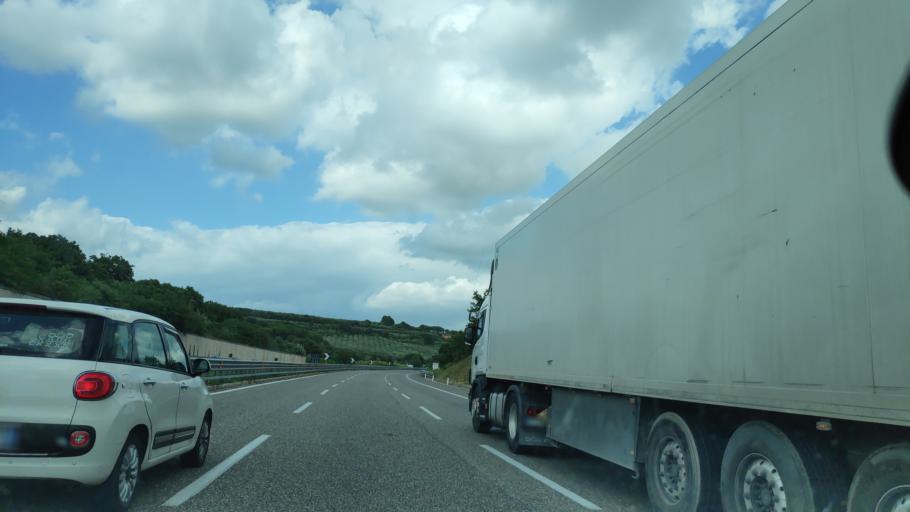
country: IT
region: Campania
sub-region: Provincia di Salerno
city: Quadrivio
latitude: 40.6121
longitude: 15.1390
